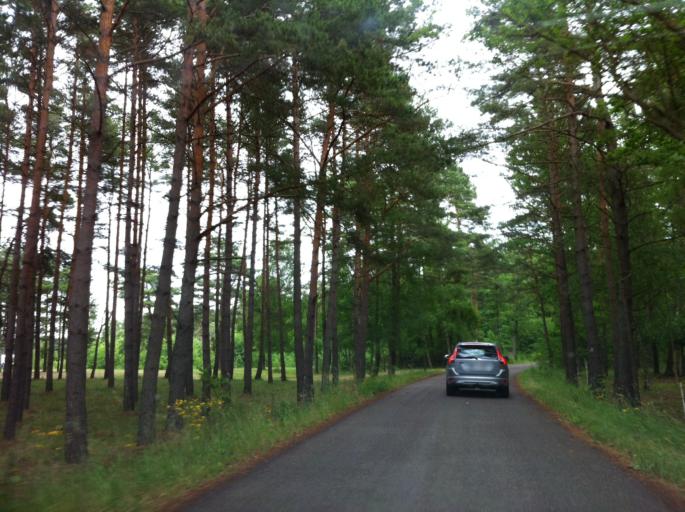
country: SE
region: Kalmar
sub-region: Vasterviks Kommun
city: Vaestervik
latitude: 57.3346
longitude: 17.0939
